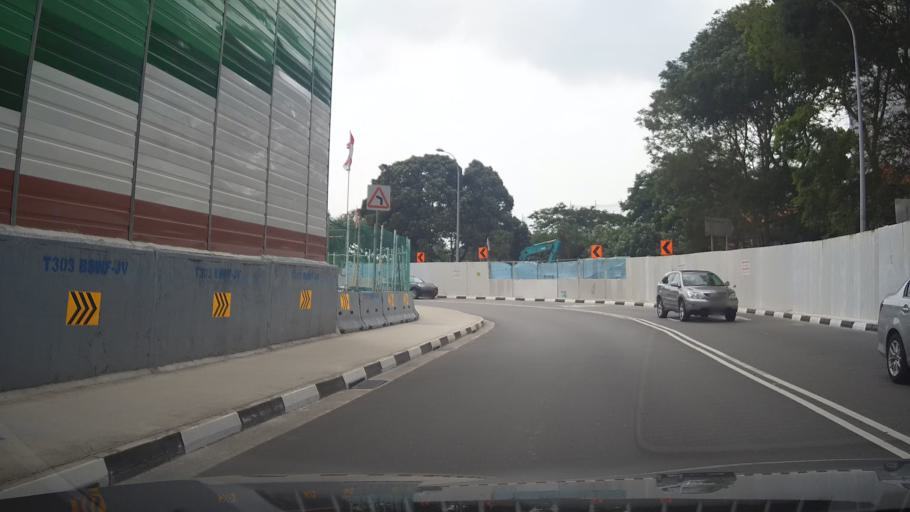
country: SG
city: Singapore
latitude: 1.2967
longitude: 103.8731
